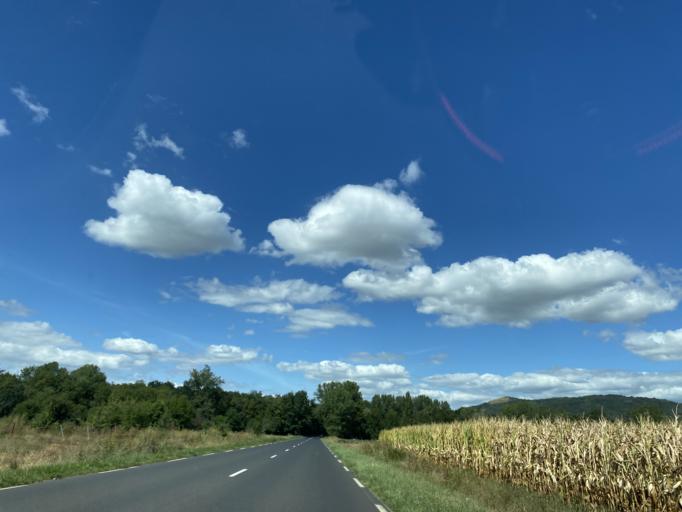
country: FR
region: Auvergne
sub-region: Departement du Puy-de-Dome
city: Perignat-sur-Allier
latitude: 45.7375
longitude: 3.2301
